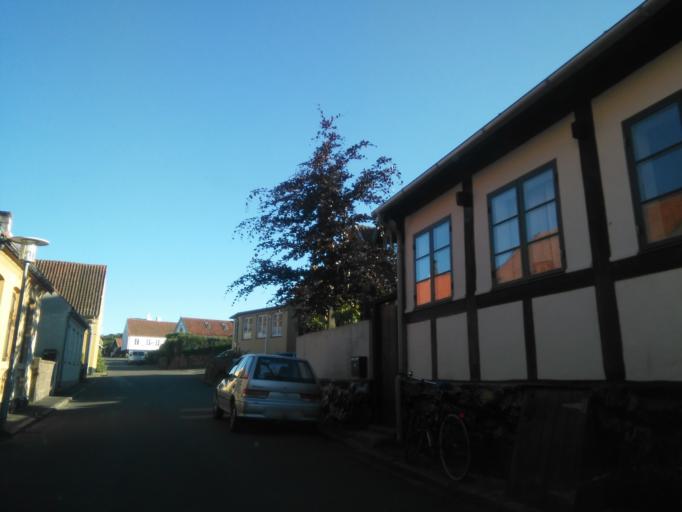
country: DK
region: Capital Region
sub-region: Bornholm Kommune
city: Ronne
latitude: 55.2741
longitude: 14.8030
